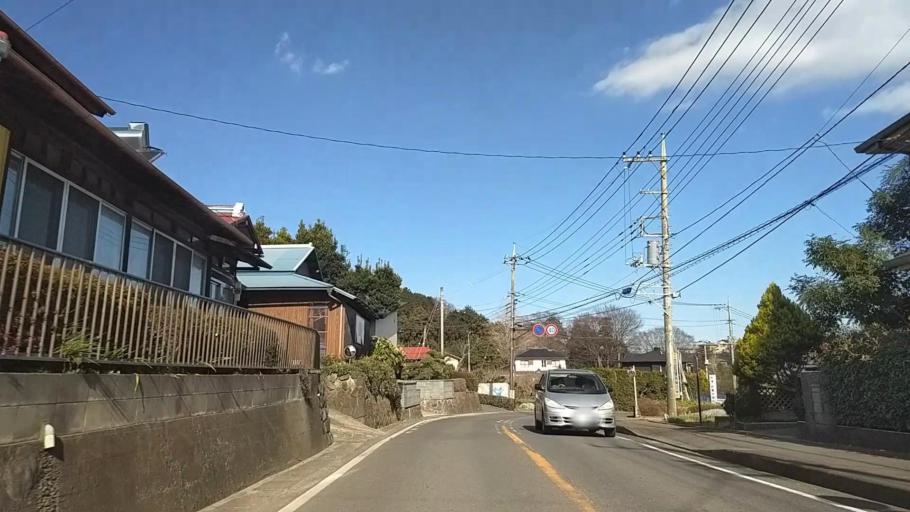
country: JP
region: Kanagawa
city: Isehara
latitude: 35.4187
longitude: 139.2880
